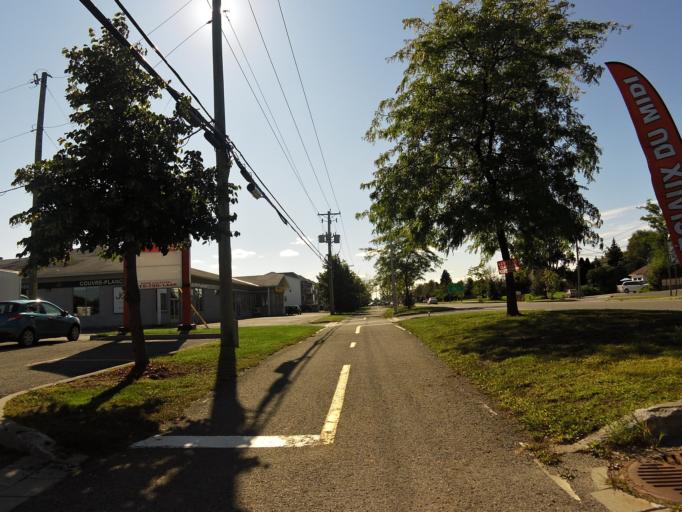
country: CA
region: Ontario
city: Clarence-Rockland
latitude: 45.5223
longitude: -75.4930
